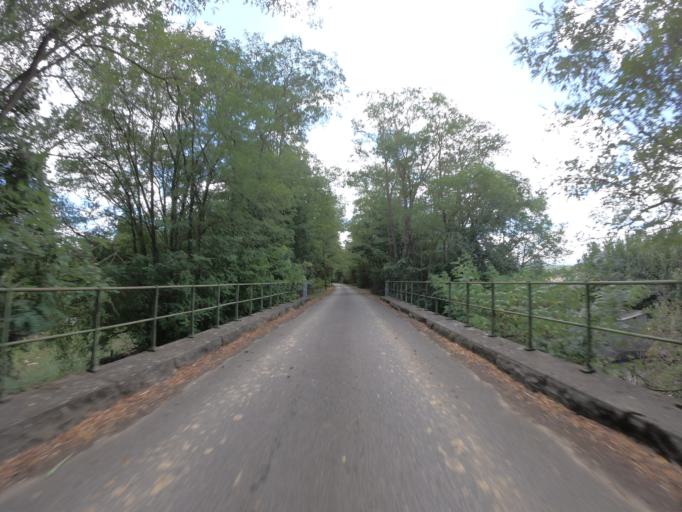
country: FR
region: Midi-Pyrenees
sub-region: Departement de l'Ariege
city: La Tour-du-Crieu
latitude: 43.0991
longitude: 1.7307
